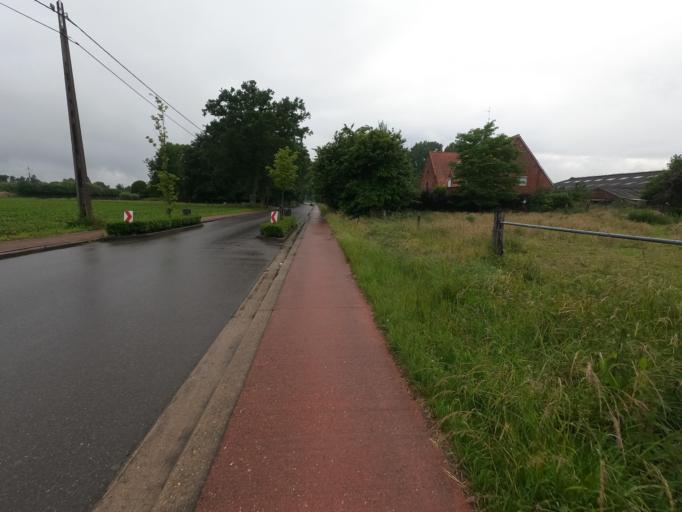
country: BE
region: Flanders
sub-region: Provincie Antwerpen
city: Kalmthout
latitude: 51.3739
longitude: 4.5118
